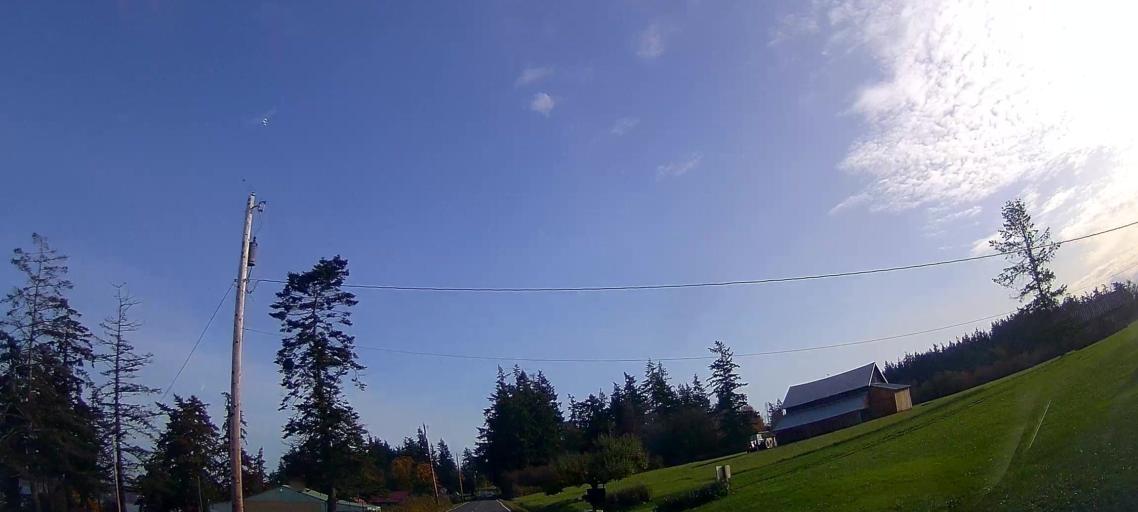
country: US
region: Washington
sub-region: Snohomish County
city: Stanwood
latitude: 48.2531
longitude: -122.4209
